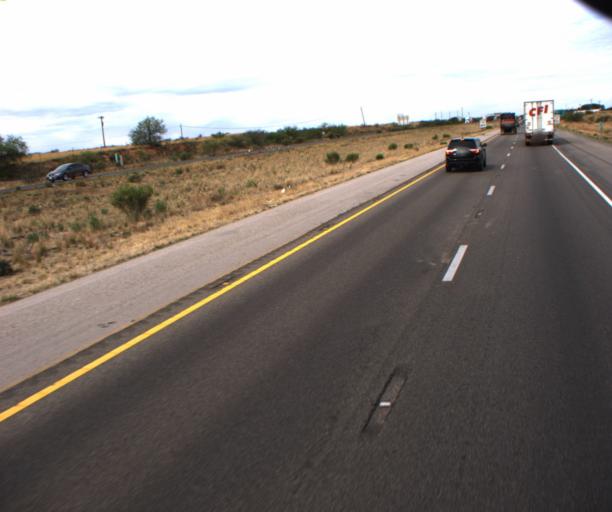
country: US
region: Arizona
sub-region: Cochise County
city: Whetstone
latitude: 31.9634
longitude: -110.3688
